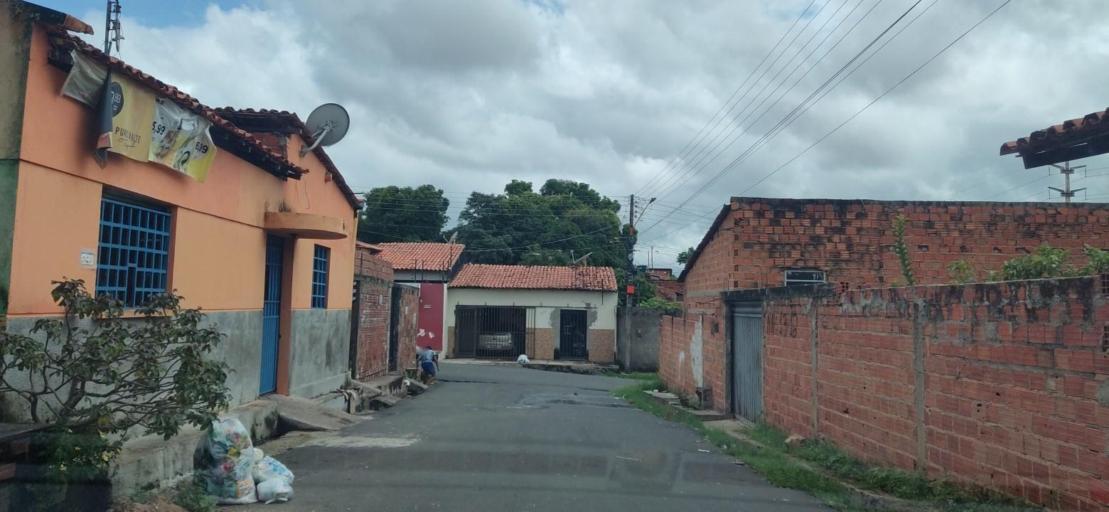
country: BR
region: Piaui
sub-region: Teresina
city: Teresina
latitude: -5.0663
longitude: -42.7520
